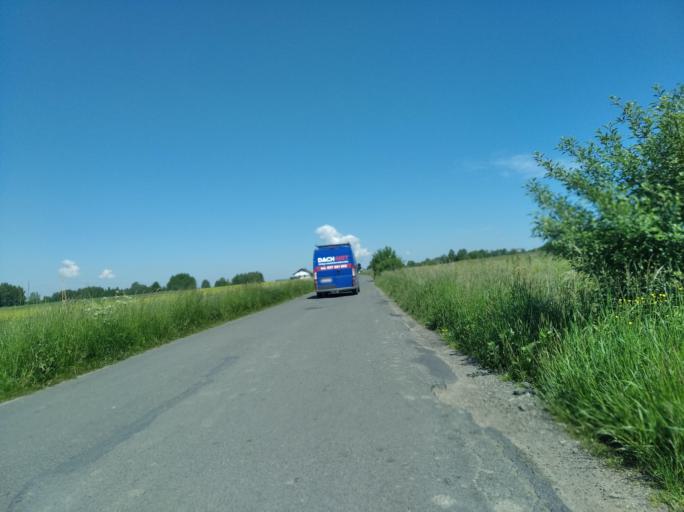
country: PL
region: Subcarpathian Voivodeship
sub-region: Powiat krosnienski
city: Odrzykon
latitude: 49.7295
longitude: 21.7524
